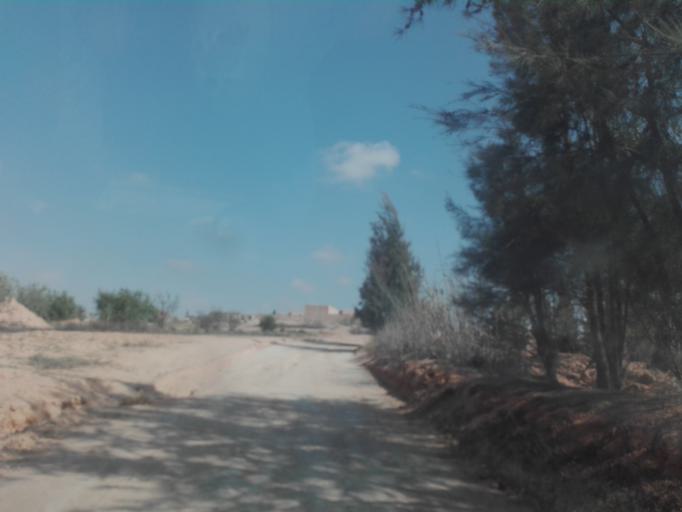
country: TN
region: Madanin
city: Medenine
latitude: 33.4382
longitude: 10.4317
